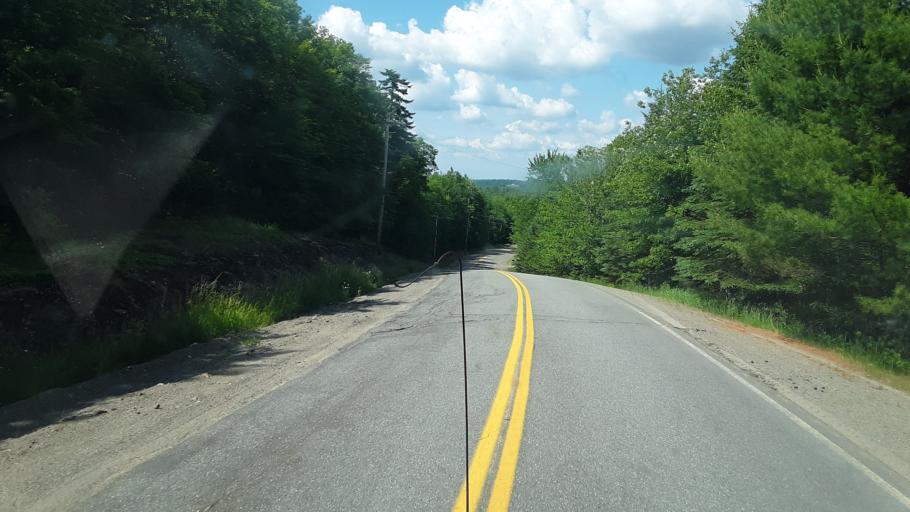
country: US
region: Maine
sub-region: Washington County
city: Calais
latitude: 45.1063
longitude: -67.5084
